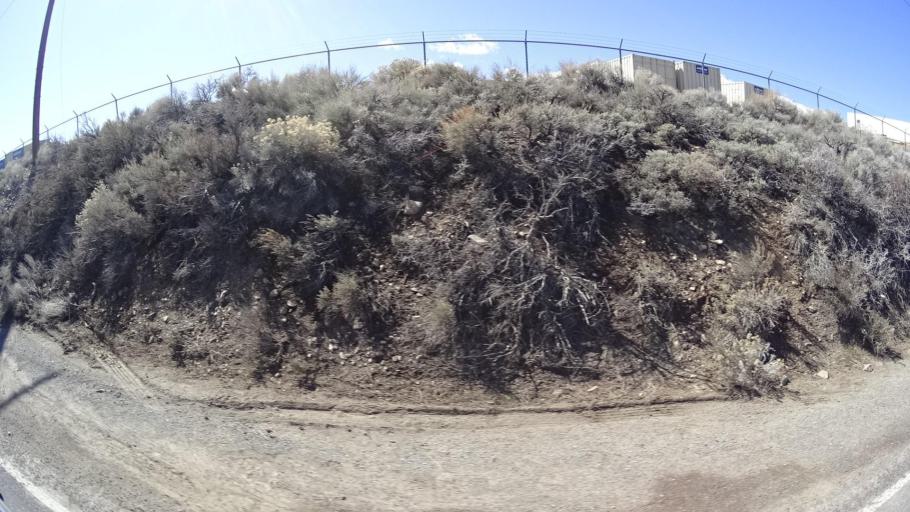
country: US
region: Nevada
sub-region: Washoe County
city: Lemmon Valley
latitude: 39.6190
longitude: -119.8903
